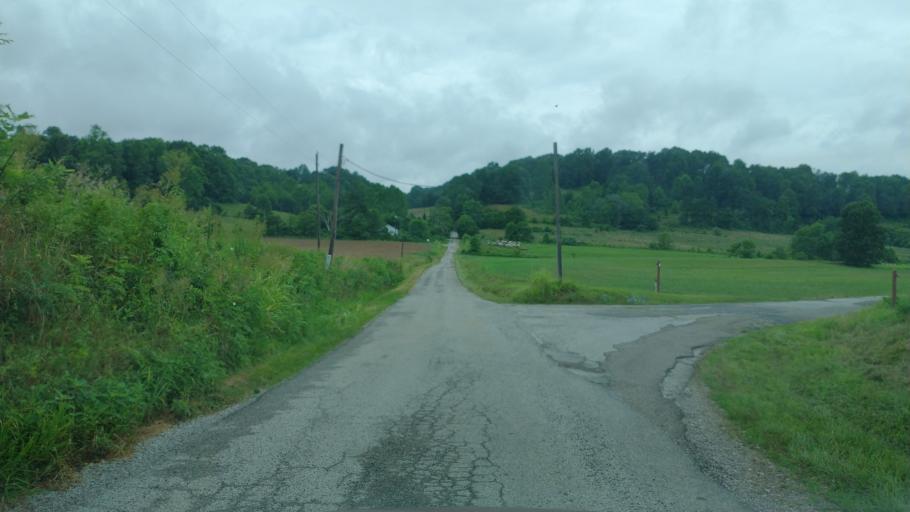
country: US
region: West Virginia
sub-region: Mason County
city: New Haven
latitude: 38.9248
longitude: -81.9757
